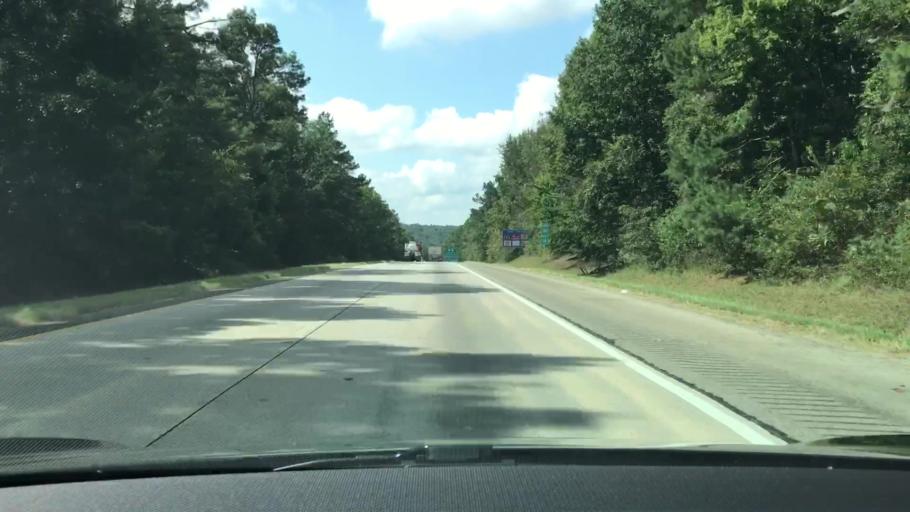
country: US
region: Georgia
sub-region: Hall County
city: Oakwood
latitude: 34.2430
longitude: -83.8386
